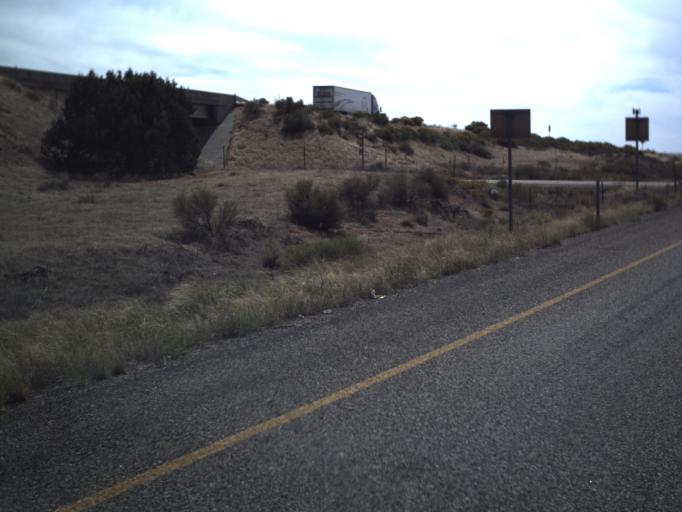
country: US
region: Colorado
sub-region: Mesa County
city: Loma
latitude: 39.1753
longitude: -109.1278
